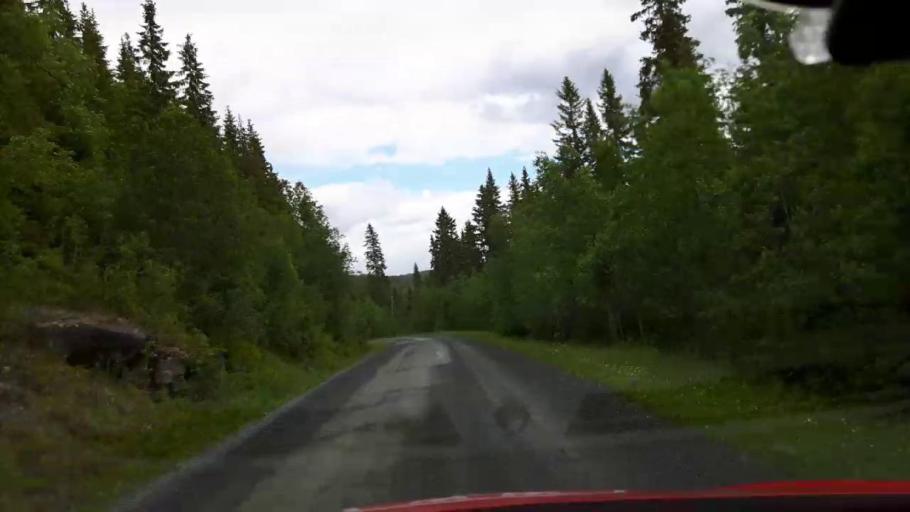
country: NO
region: Nord-Trondelag
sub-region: Lierne
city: Sandvika
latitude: 64.1592
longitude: 14.0435
